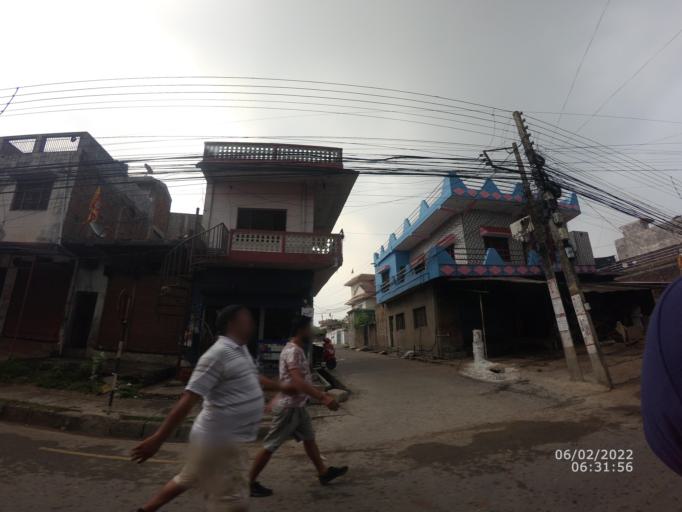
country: NP
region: Western Region
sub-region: Lumbini Zone
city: Bhairahawa
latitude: 27.5019
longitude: 83.4494
